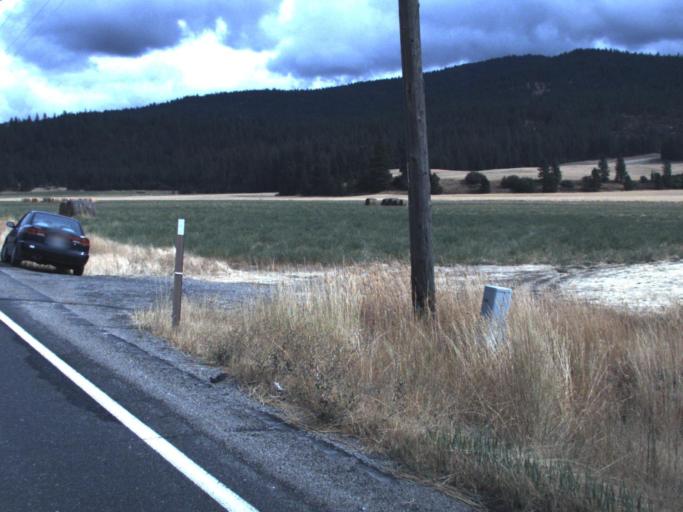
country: US
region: Washington
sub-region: Spokane County
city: Deer Park
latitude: 47.9190
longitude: -117.7904
